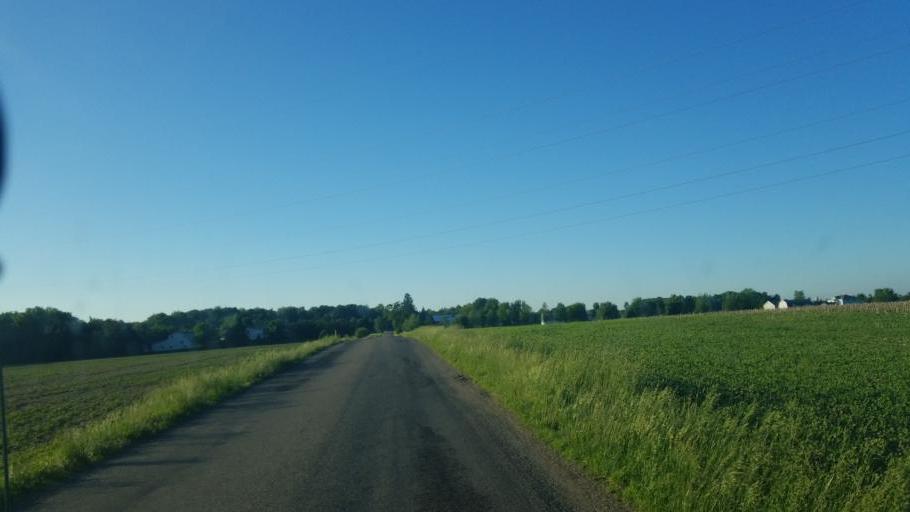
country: US
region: Indiana
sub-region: Elkhart County
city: Nappanee
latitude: 41.4270
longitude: -86.0493
